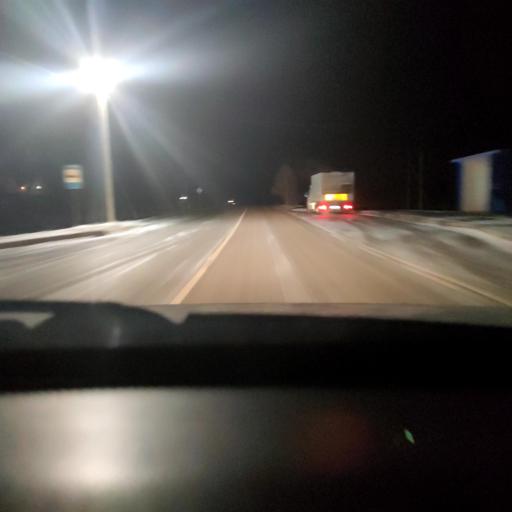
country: RU
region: Perm
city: Ust'-Kachka
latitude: 57.9902
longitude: 55.7144
